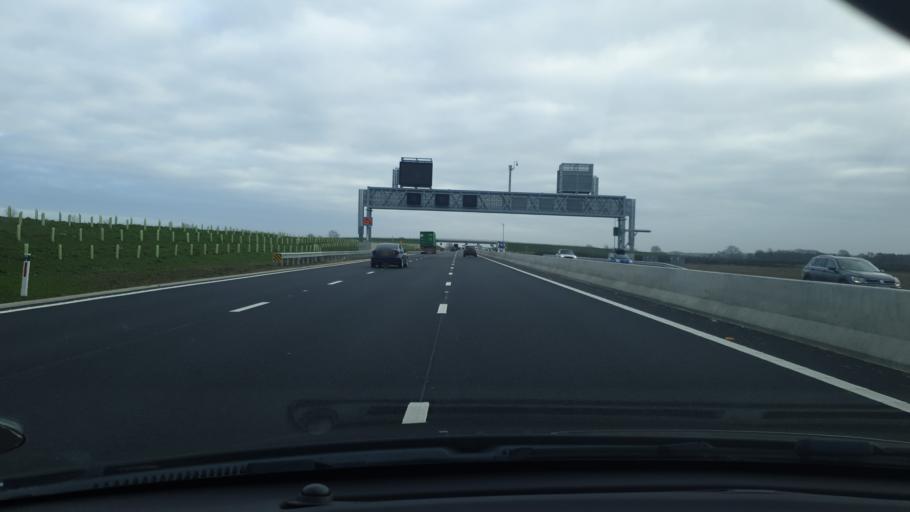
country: GB
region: England
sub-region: Cambridgeshire
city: Hemingford Grey
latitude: 52.2900
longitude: -0.0788
